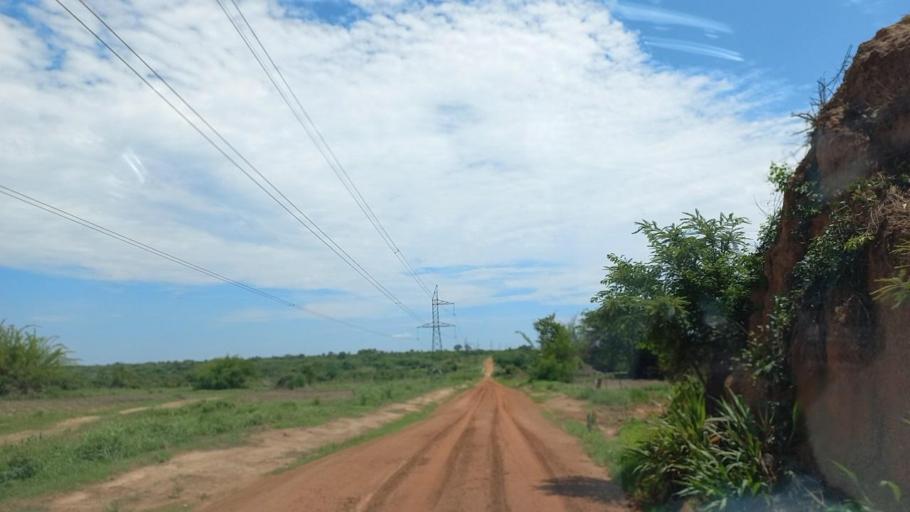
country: ZM
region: Copperbelt
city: Kitwe
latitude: -12.8334
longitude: 28.3443
